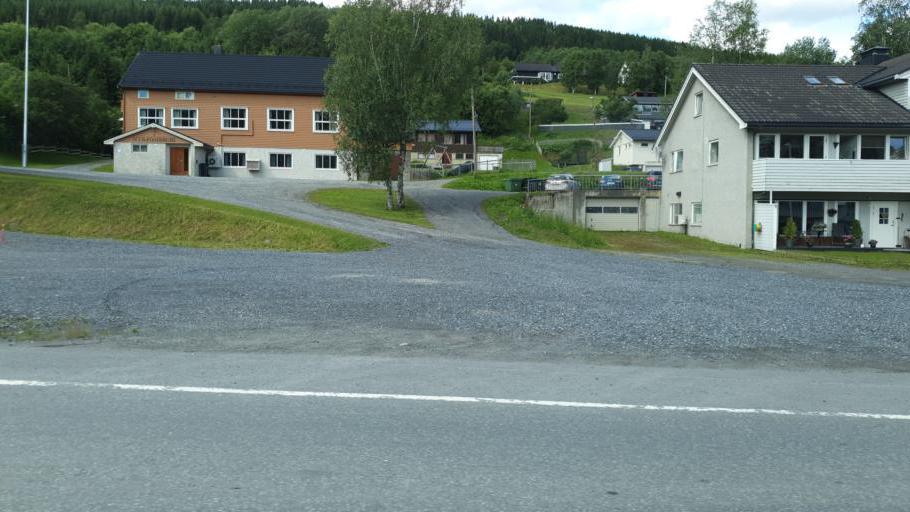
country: NO
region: Sor-Trondelag
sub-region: Midtre Gauldal
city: Storen
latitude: 62.9470
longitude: 10.1896
